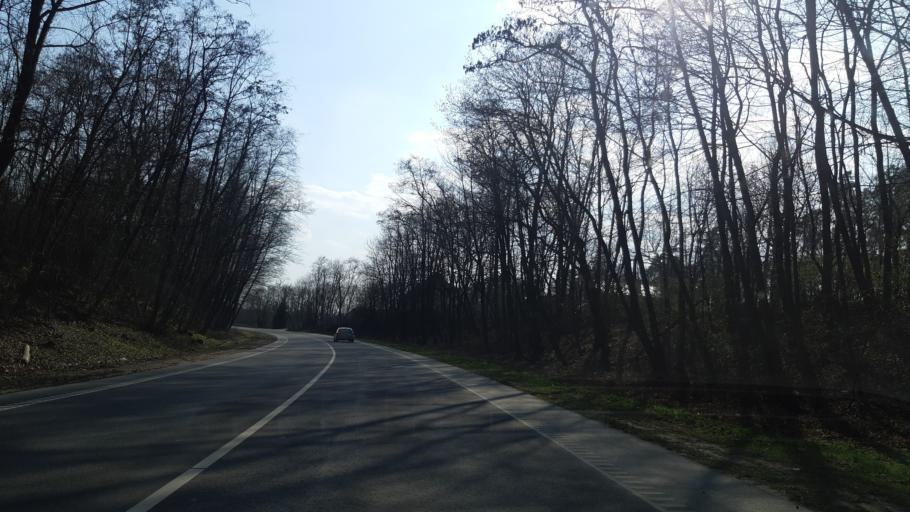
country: LT
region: Kauno apskritis
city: Dainava (Kaunas)
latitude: 54.8696
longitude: 23.9882
